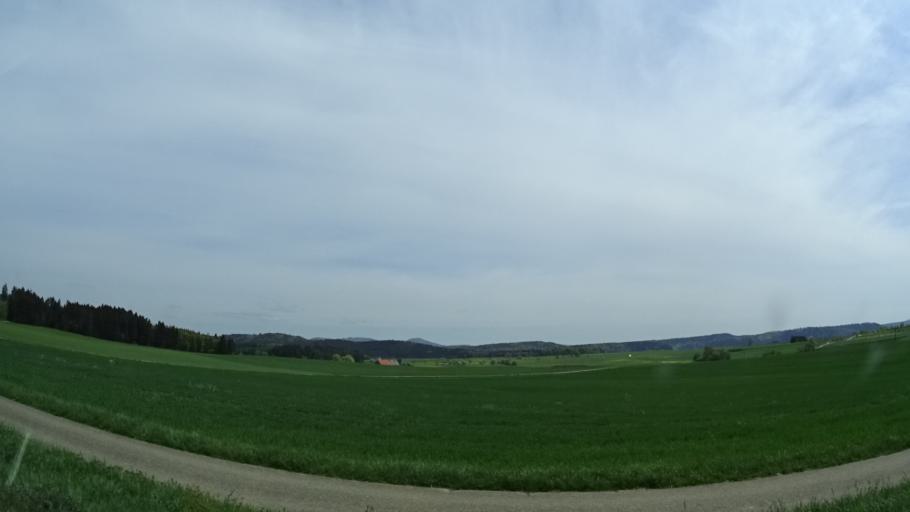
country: DE
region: Baden-Wuerttemberg
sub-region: Freiburg Region
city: Dietingen
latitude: 48.1887
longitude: 8.6378
